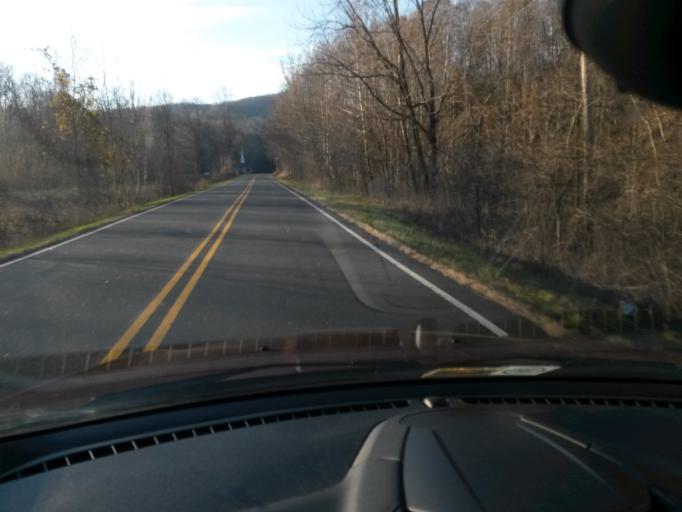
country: US
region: Virginia
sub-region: City of Buena Vista
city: Buena Vista
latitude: 37.6673
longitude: -79.2076
